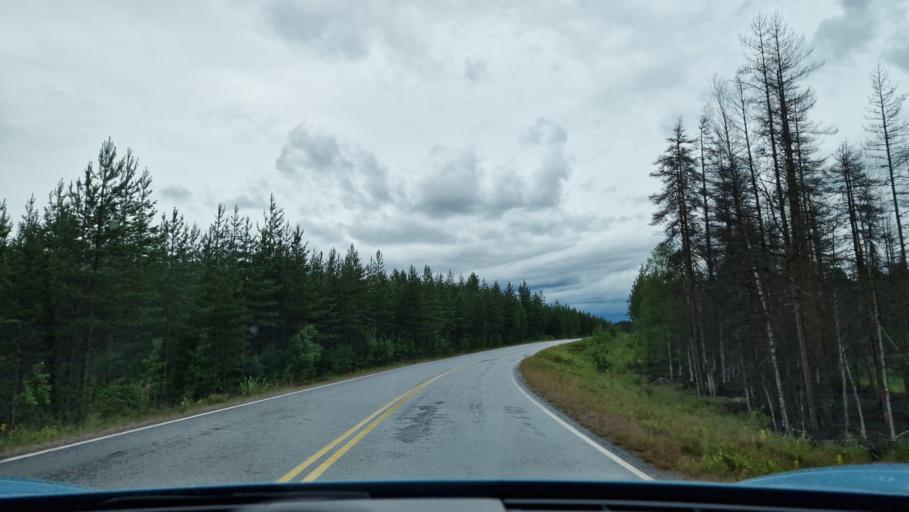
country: FI
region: Central Finland
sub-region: Saarijaervi-Viitasaari
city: Pylkoenmaeki
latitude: 62.6652
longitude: 24.5425
